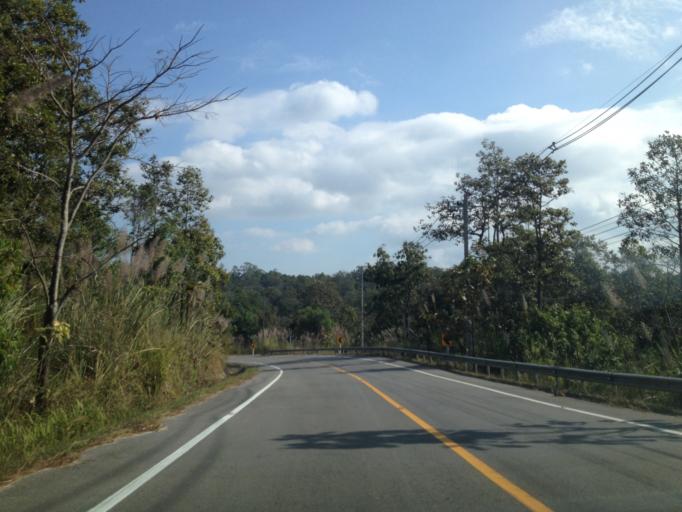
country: TH
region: Mae Hong Son
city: Pa Pae
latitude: 18.1588
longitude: 98.2780
